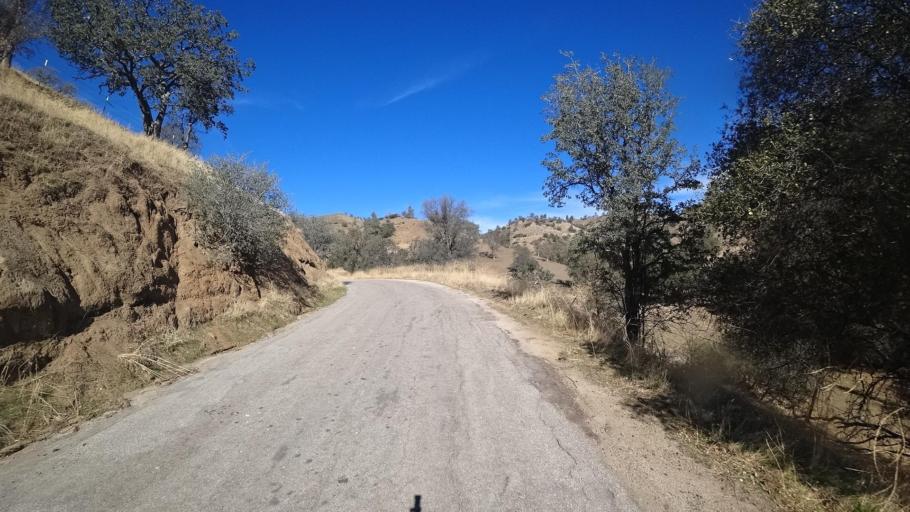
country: US
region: California
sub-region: Kern County
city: Arvin
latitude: 35.4329
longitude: -118.7295
